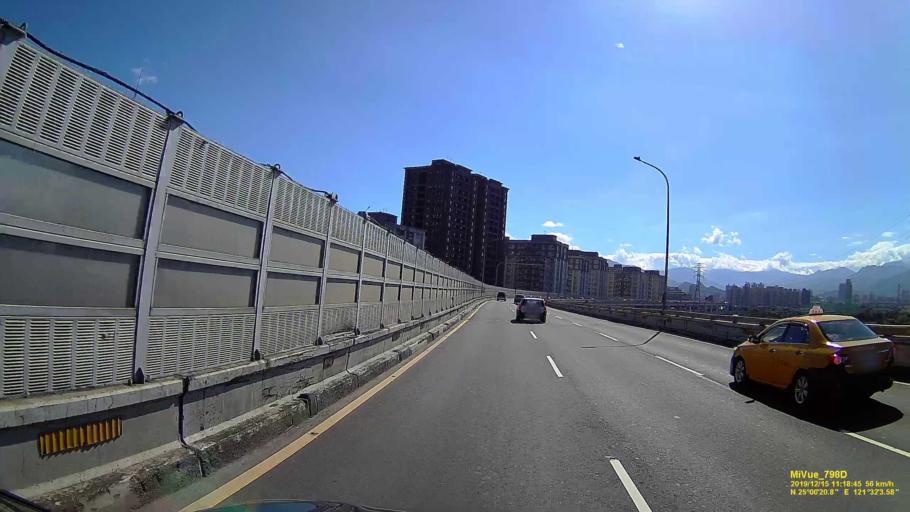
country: TW
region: Taipei
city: Taipei
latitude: 25.0056
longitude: 121.5344
